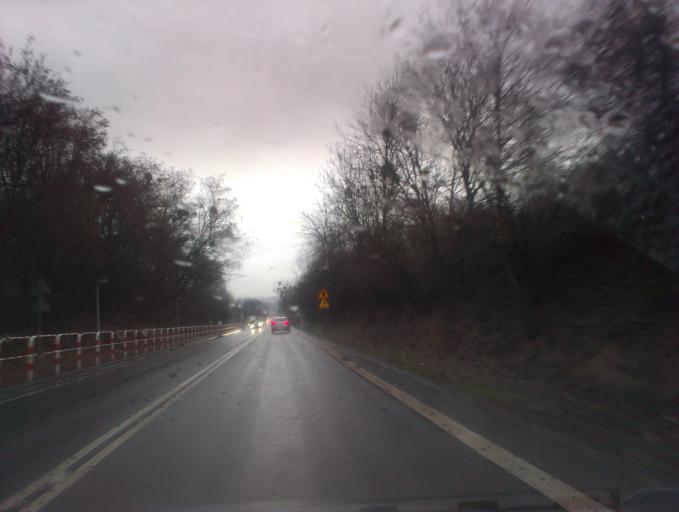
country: PL
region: Greater Poland Voivodeship
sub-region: Powiat obornicki
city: Oborniki
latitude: 52.6314
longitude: 16.8096
